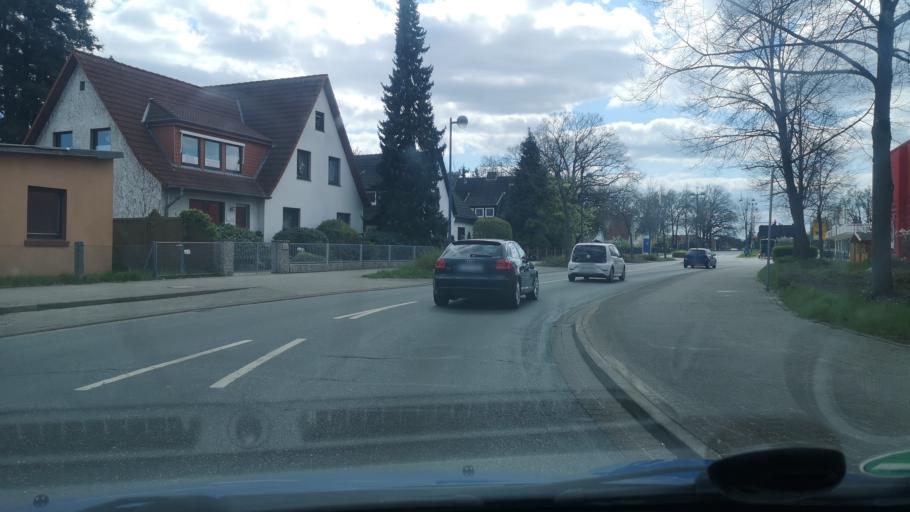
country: DE
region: Lower Saxony
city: Celle
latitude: 52.6082
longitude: 10.0641
